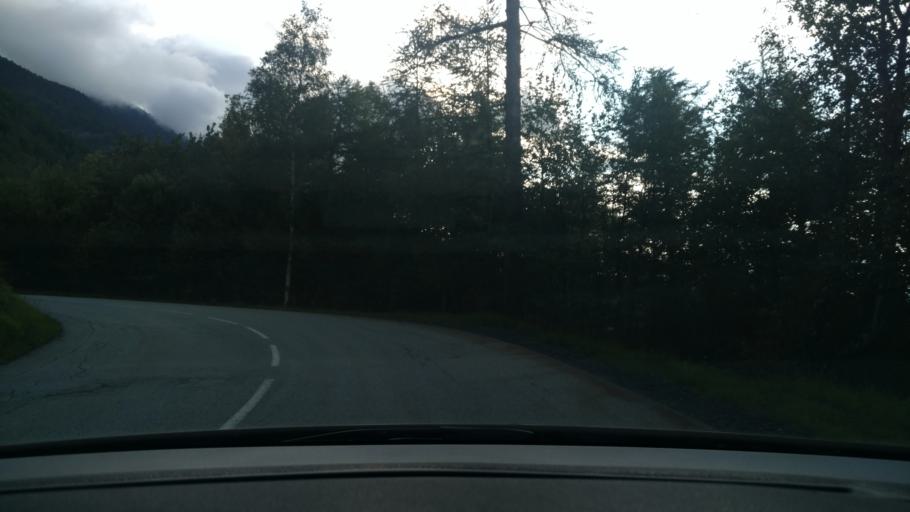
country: FR
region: Rhone-Alpes
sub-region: Departement de la Savoie
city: Villargondran
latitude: 45.2407
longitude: 6.4103
